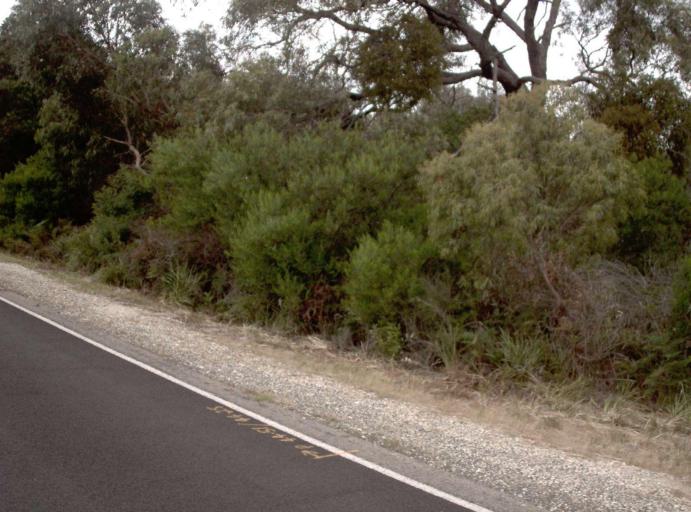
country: AU
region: Victoria
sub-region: East Gippsland
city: Bairnsdale
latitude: -38.0967
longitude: 147.5107
